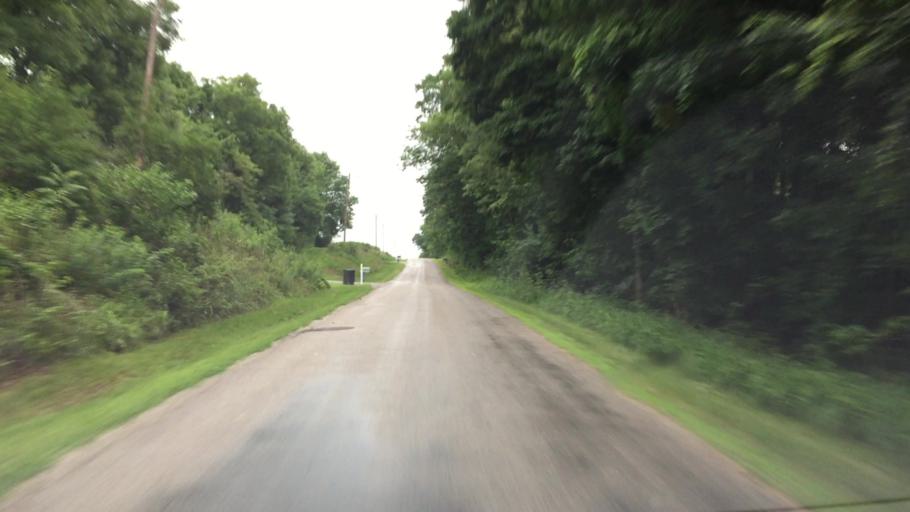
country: US
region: Iowa
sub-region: Lee County
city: Keokuk
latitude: 40.4263
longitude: -91.3637
